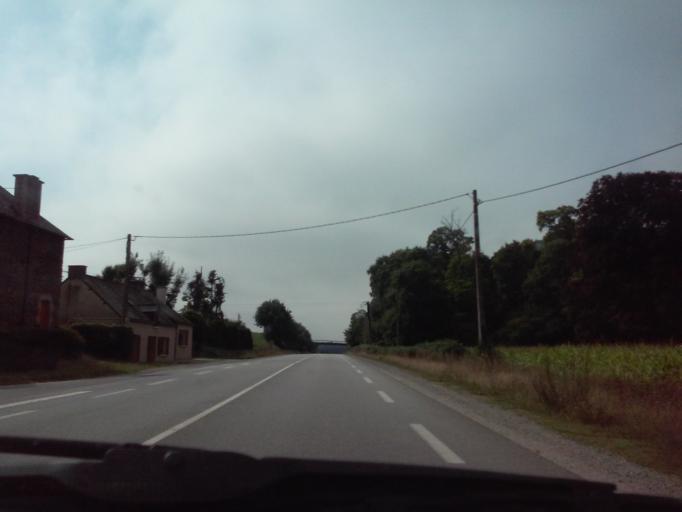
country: FR
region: Brittany
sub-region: Departement du Morbihan
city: Loyat
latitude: 47.9696
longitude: -2.3828
